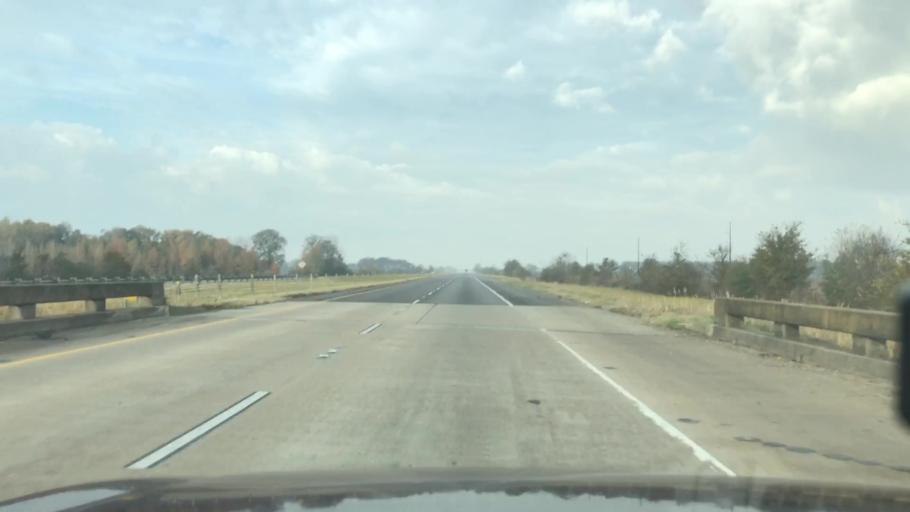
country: US
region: Louisiana
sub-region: Madison Parish
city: Tallulah
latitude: 32.4210
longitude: -91.3205
